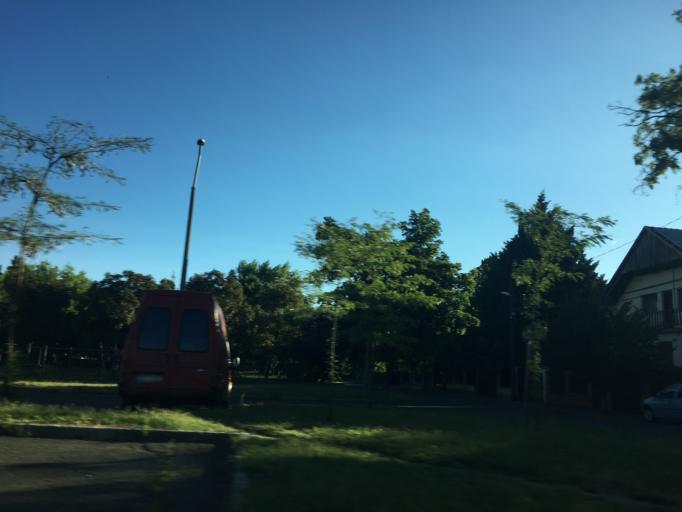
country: HU
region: Budapest
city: Budapest XVII. keruelet
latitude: 47.4755
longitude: 19.2562
